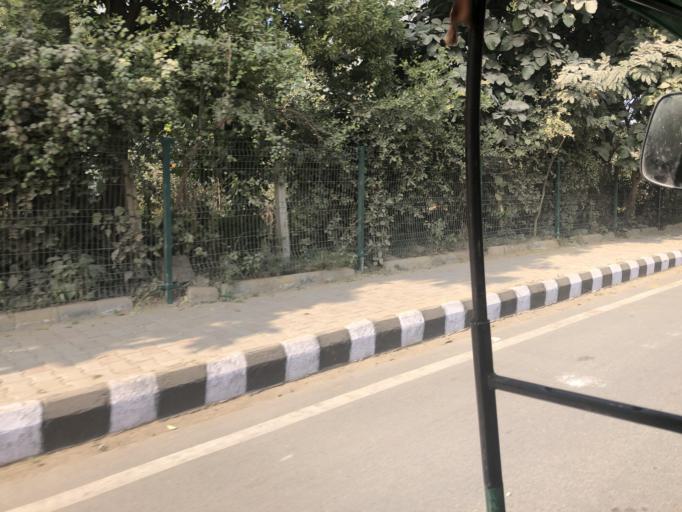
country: IN
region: Haryana
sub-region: Gurgaon
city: Gurgaon
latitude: 28.4345
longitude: 77.0906
